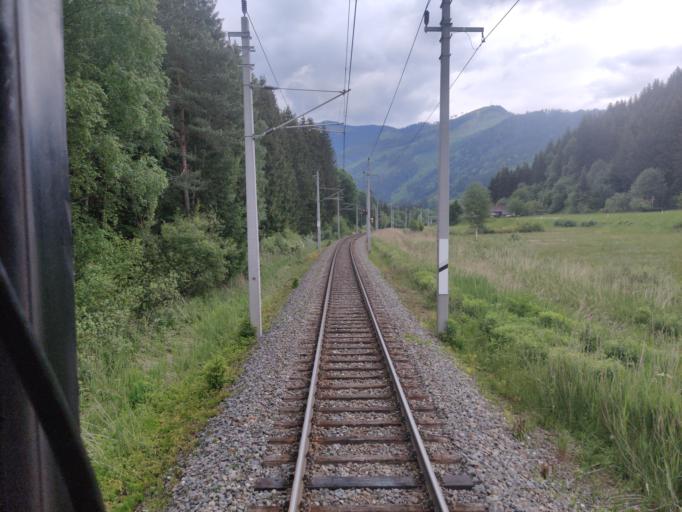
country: AT
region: Styria
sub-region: Politischer Bezirk Liezen
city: Lassing
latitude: 47.5497
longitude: 14.2917
